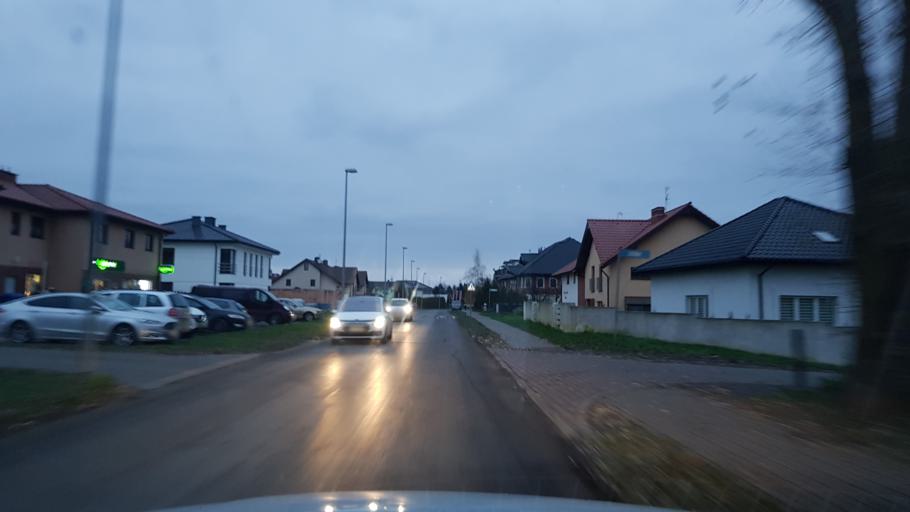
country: PL
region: West Pomeranian Voivodeship
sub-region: Powiat policki
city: Przeclaw
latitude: 53.4333
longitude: 14.4674
